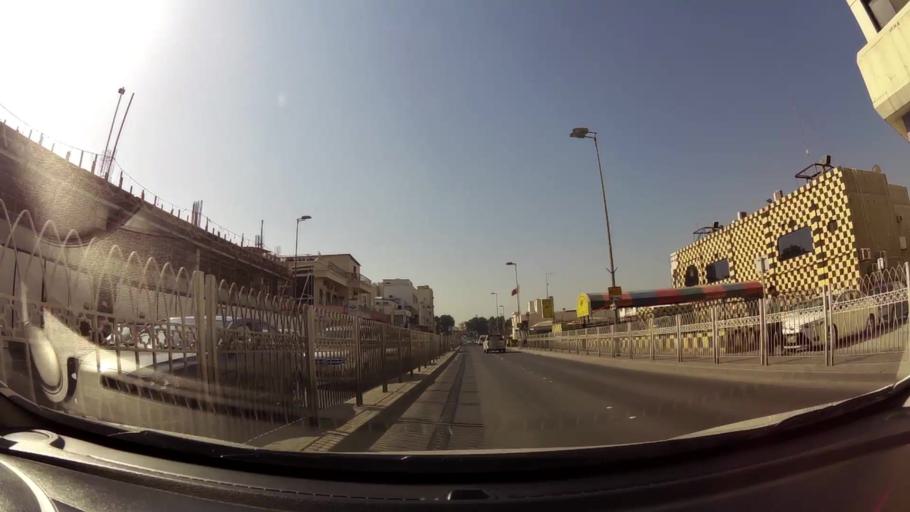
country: BH
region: Manama
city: Manama
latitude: 26.2260
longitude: 50.5878
